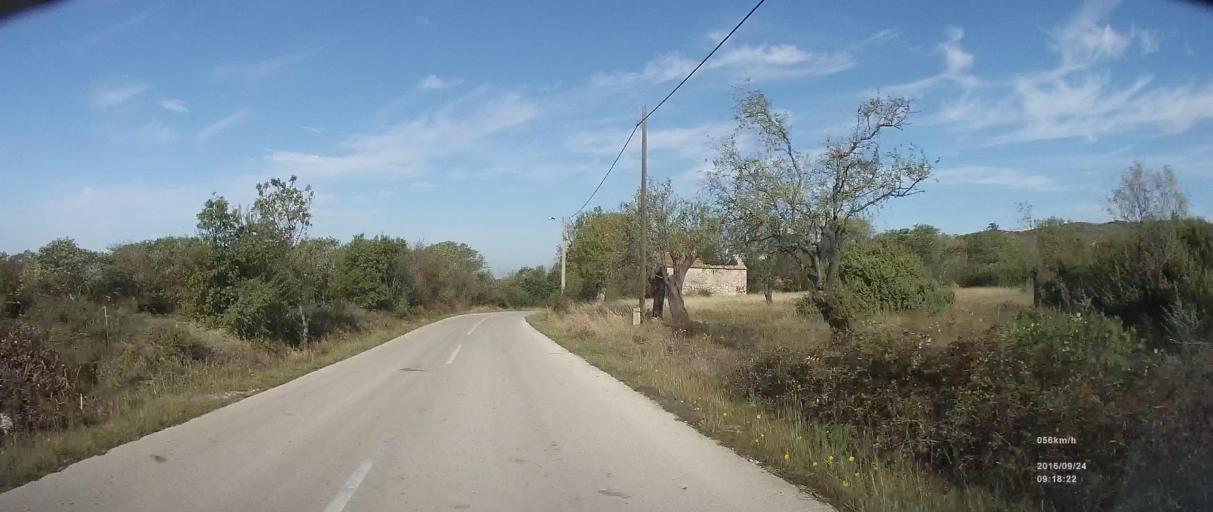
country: HR
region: Zadarska
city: Polaca
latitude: 44.0560
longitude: 15.5126
